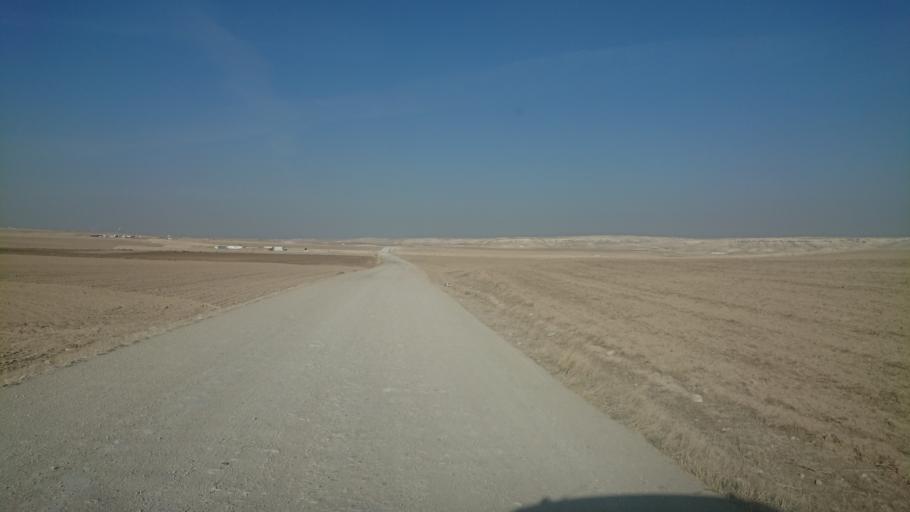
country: TR
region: Aksaray
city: Sultanhani
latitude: 38.0641
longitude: 33.6153
